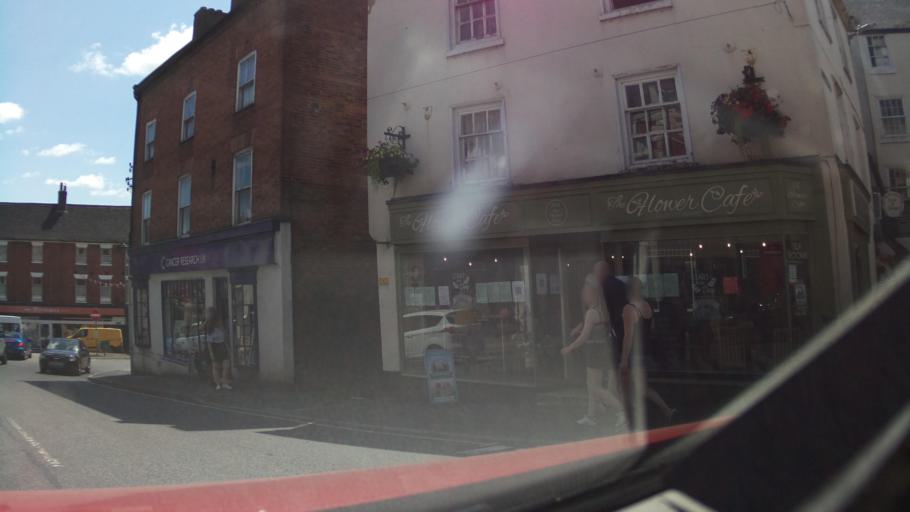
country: GB
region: England
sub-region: Derbyshire
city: Ashbourne
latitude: 53.0181
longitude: -1.7323
